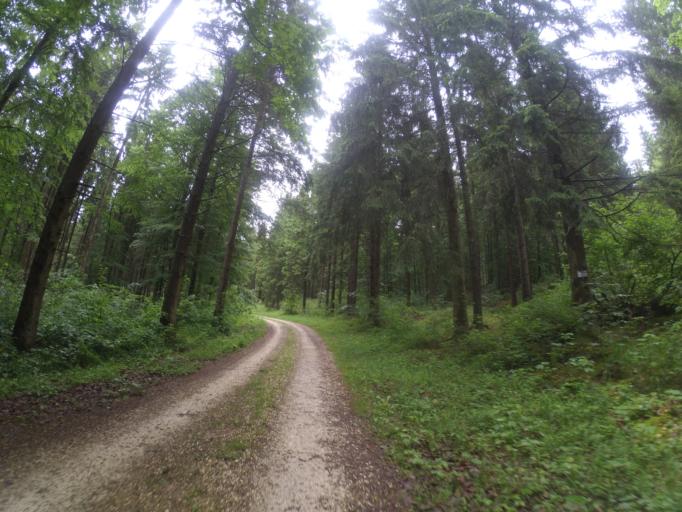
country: DE
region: Baden-Wuerttemberg
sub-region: Tuebingen Region
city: Borslingen
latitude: 48.5205
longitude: 10.0536
